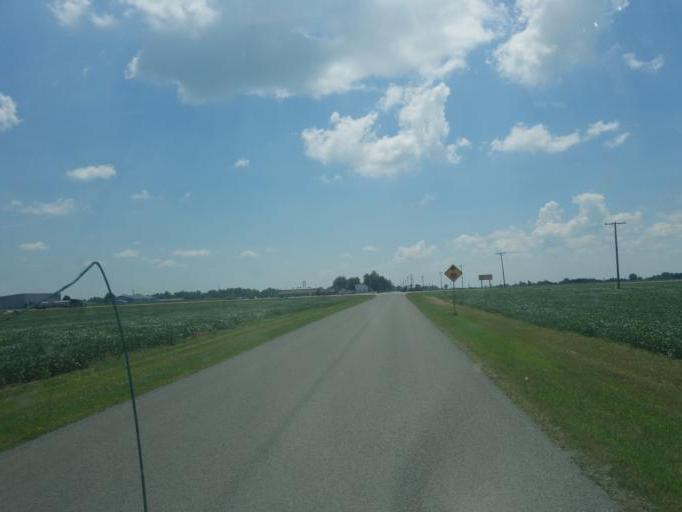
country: US
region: Ohio
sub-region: Mercer County
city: Celina
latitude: 40.5591
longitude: -84.4939
